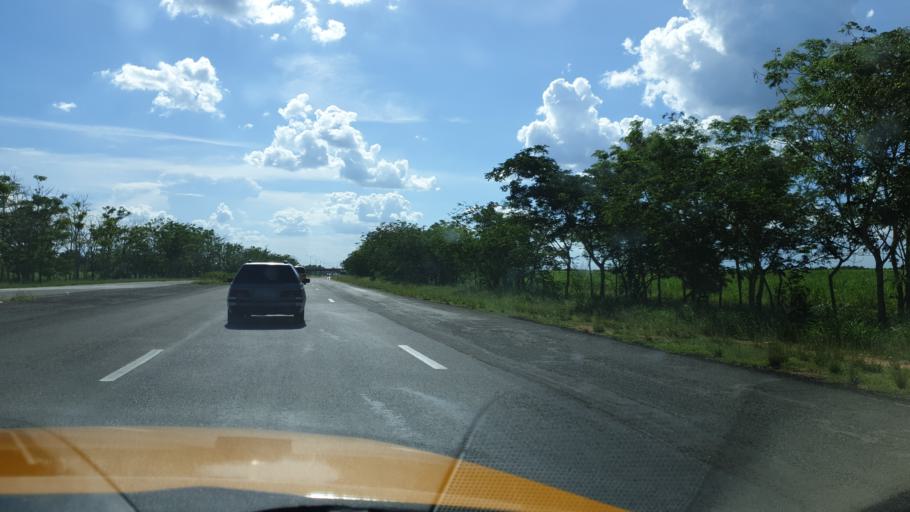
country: CU
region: Cienfuegos
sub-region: Municipio de Aguada de Pasajeros
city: Aguada de Pasajeros
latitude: 22.4024
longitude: -80.8561
